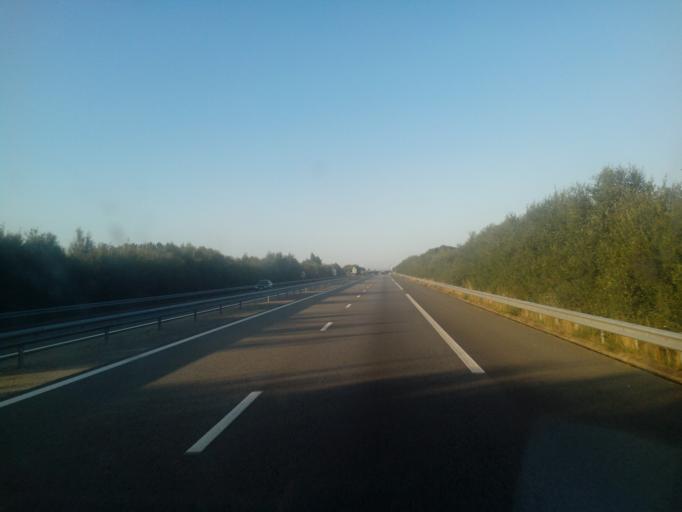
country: FR
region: Brittany
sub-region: Departement du Morbihan
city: Saint-Gonnery
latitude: 48.1168
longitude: -2.8593
